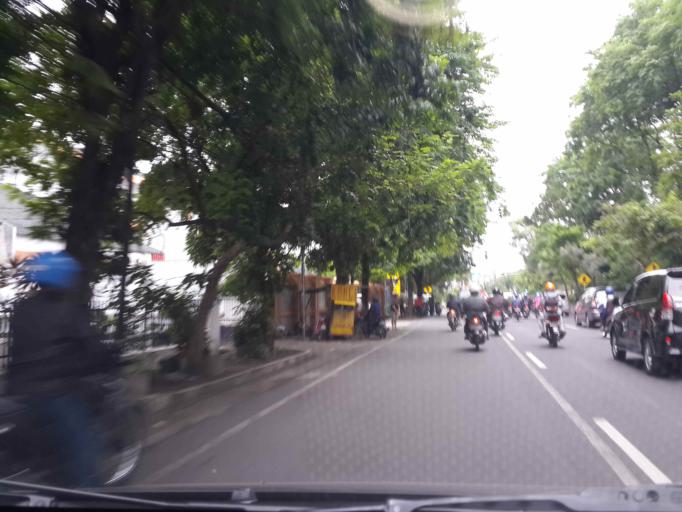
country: ID
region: East Java
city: Gubengairlangga
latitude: -7.2801
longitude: 112.7309
